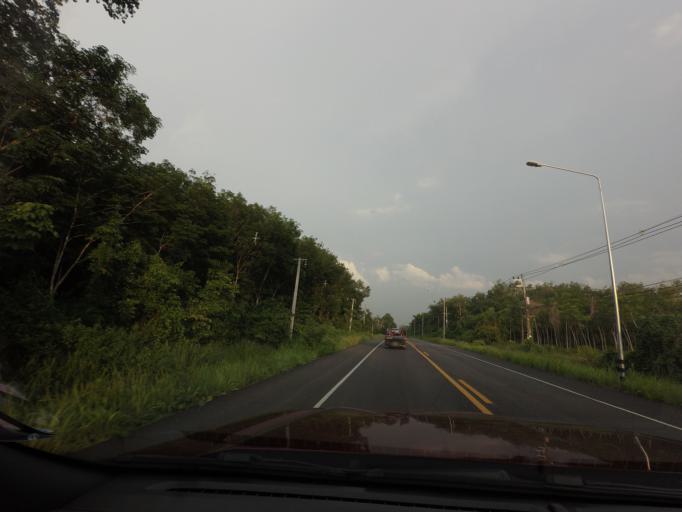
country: TH
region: Pattani
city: Mae Lan
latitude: 6.6579
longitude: 101.1708
